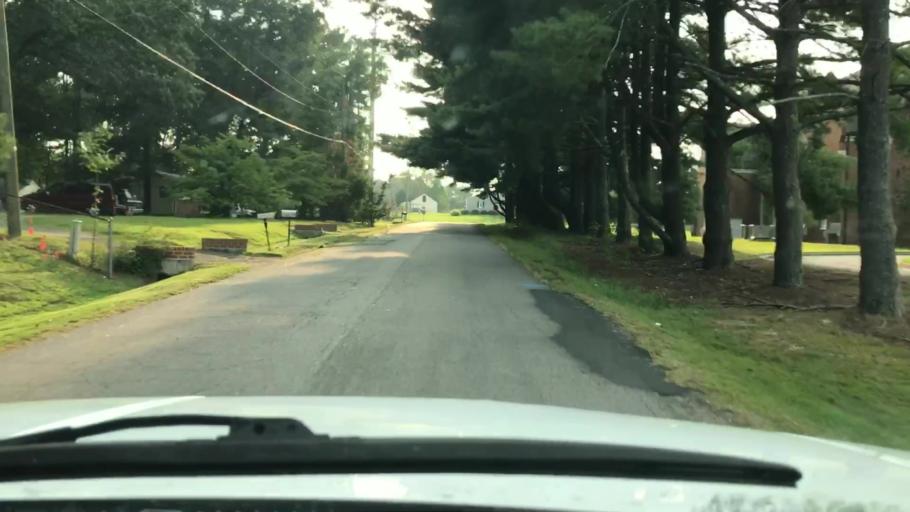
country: US
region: Virginia
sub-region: Chesterfield County
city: Chesterfield
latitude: 37.4365
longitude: -77.5235
